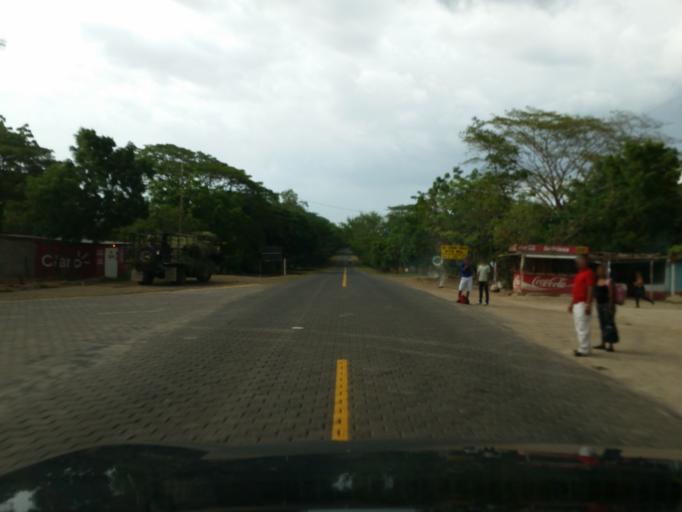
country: NI
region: Managua
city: Carlos Fonseca Amador
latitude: 11.9956
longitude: -86.5160
